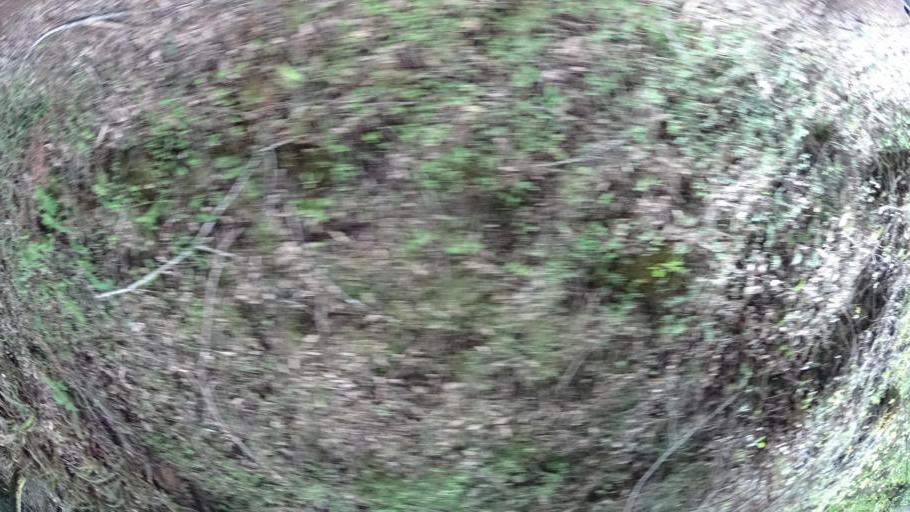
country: US
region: California
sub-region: Humboldt County
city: Blue Lake
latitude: 40.7590
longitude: -123.9195
